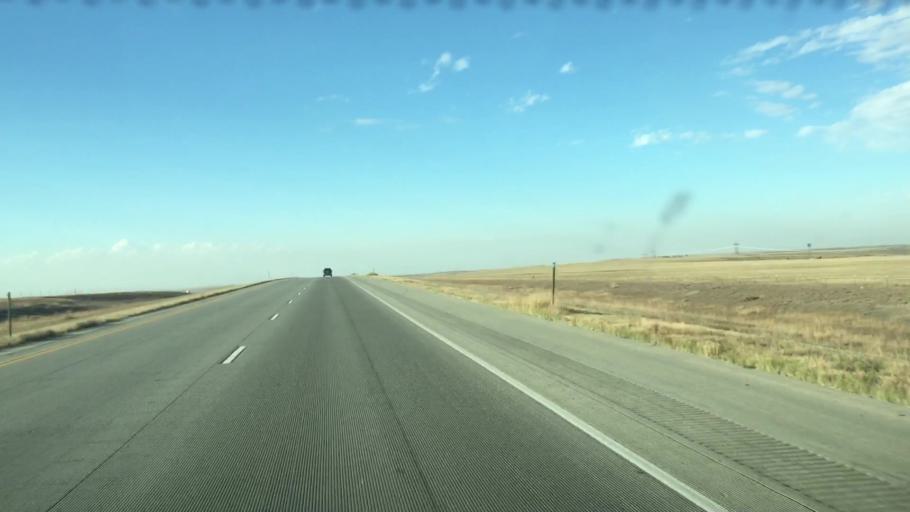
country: US
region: Colorado
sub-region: Lincoln County
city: Limon
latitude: 39.3903
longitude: -103.8890
